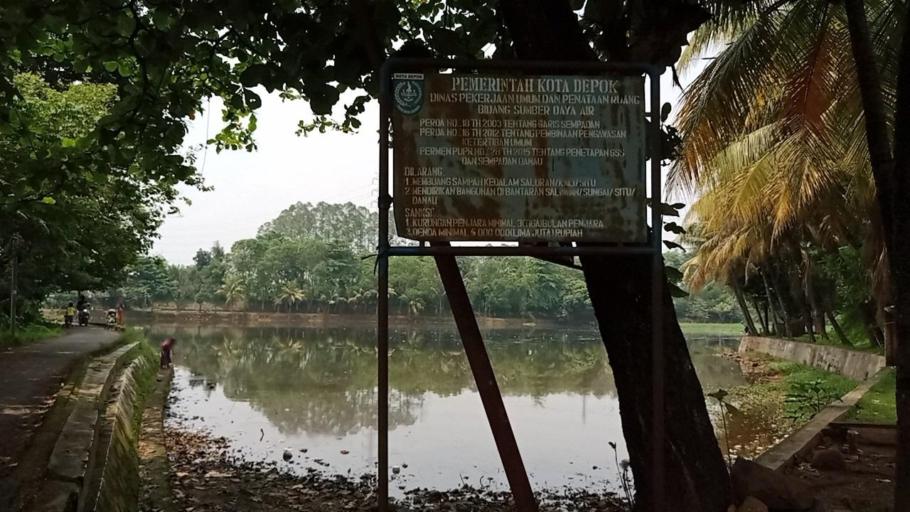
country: ID
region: West Java
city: Sawangan
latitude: -6.4116
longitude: 106.7949
